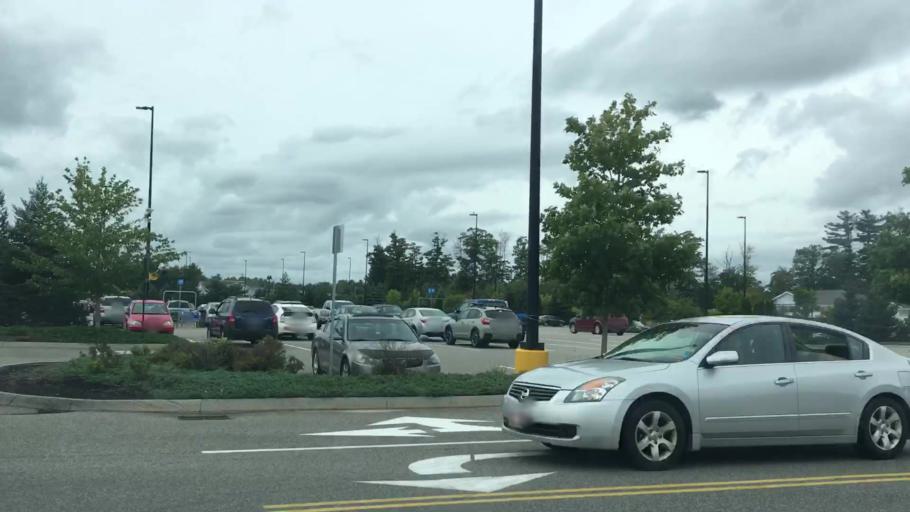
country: US
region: Maine
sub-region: Cumberland County
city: South Portland Gardens
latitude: 43.6238
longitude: -70.3423
